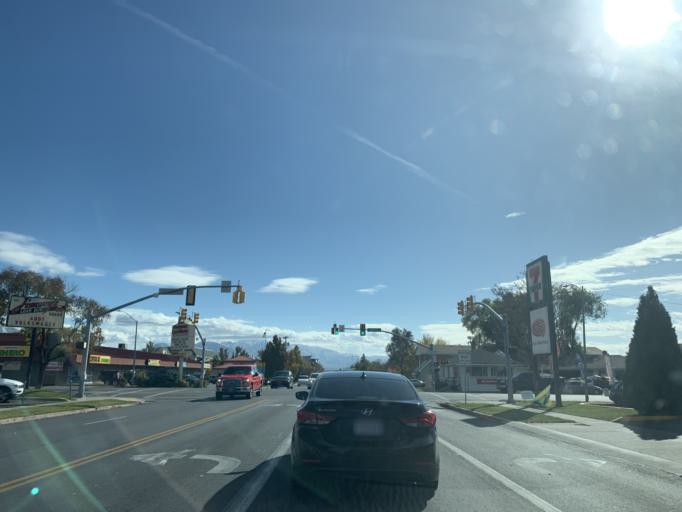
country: US
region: Utah
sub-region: Utah County
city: Provo
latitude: 40.2301
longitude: -111.6623
